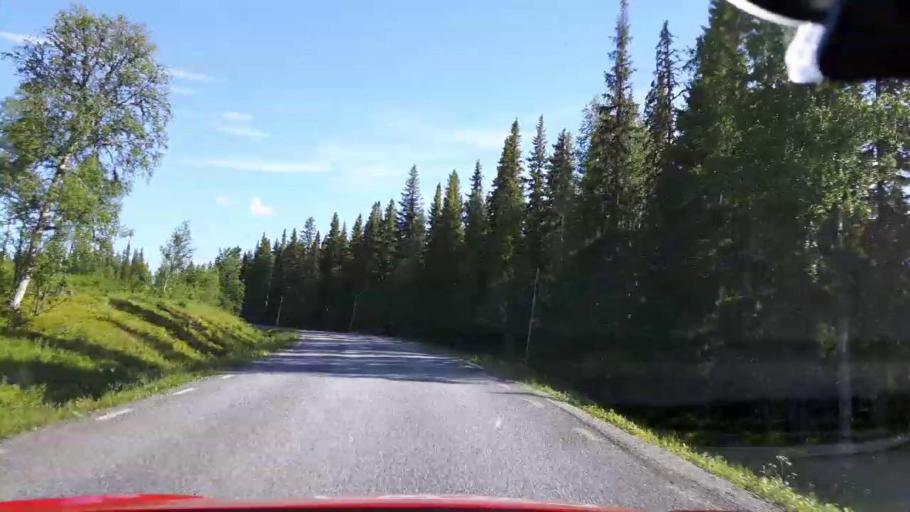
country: SE
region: Jaemtland
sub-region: Krokoms Kommun
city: Valla
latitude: 63.7232
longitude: 14.1230
